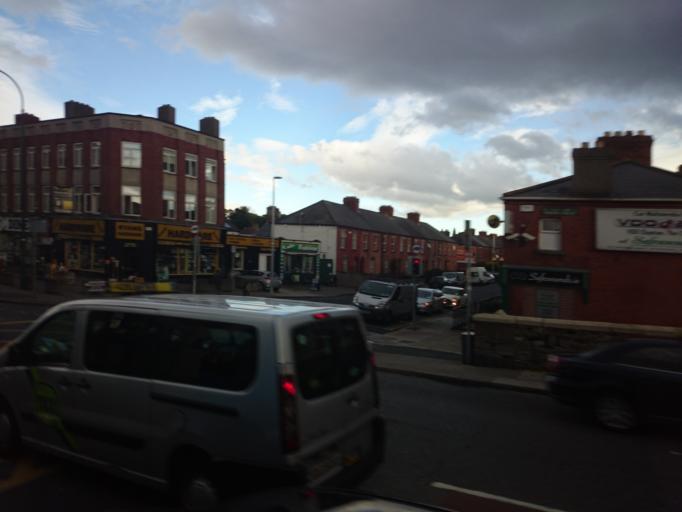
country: IE
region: Leinster
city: Drumcondra
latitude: 53.3687
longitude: -6.2550
